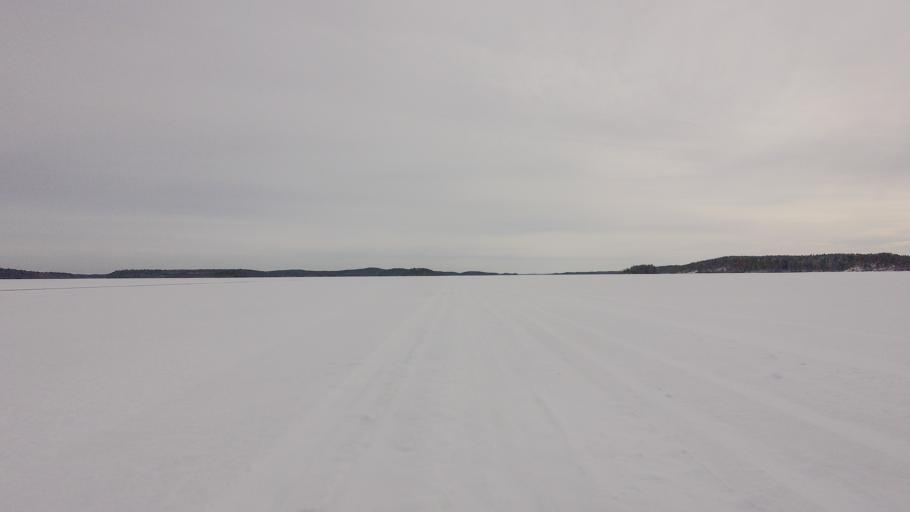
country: FI
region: Southern Savonia
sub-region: Savonlinna
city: Rantasalmi
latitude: 62.1026
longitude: 28.4356
